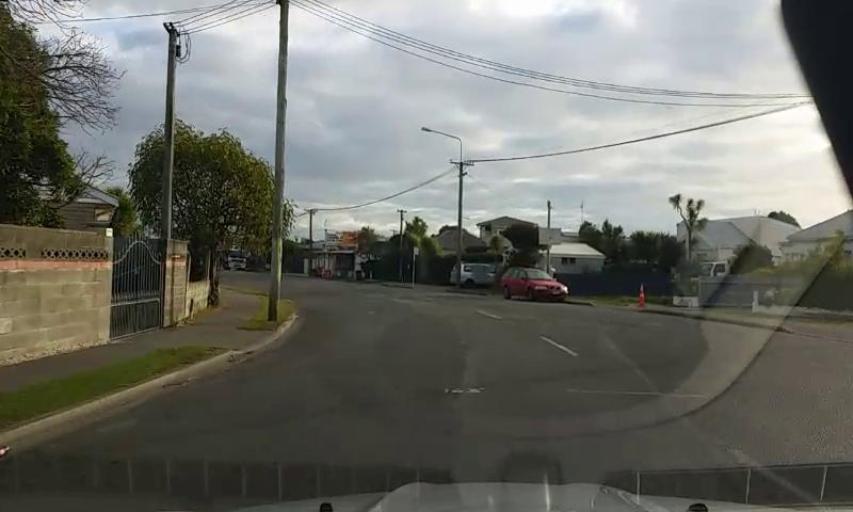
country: NZ
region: Canterbury
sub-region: Christchurch City
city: Christchurch
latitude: -43.5188
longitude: 172.7309
